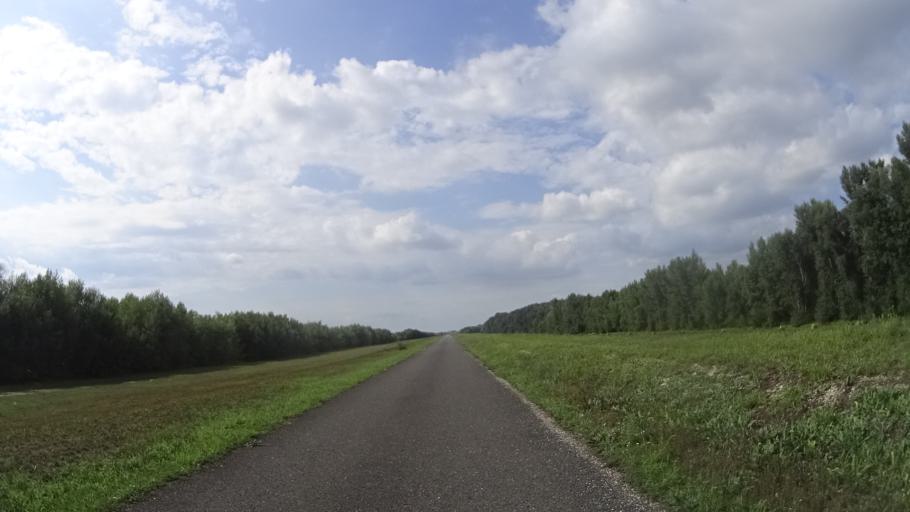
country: SK
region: Trnavsky
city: Gabcikovo
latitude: 47.8493
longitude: 17.5785
